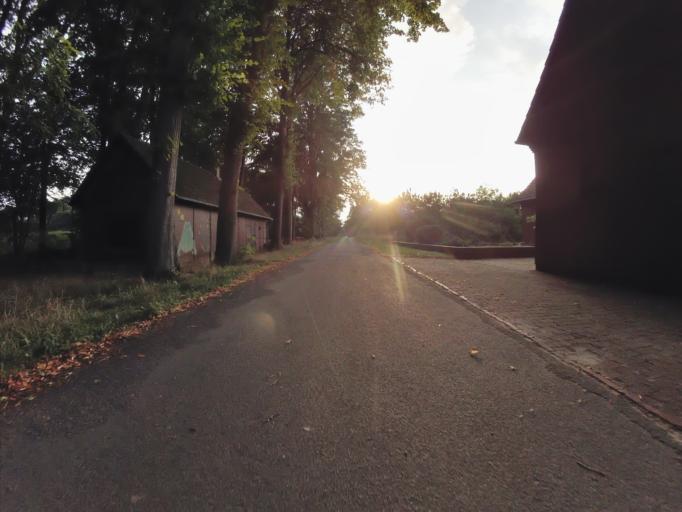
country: DE
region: North Rhine-Westphalia
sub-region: Regierungsbezirk Munster
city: Westerkappeln
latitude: 52.3380
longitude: 7.9026
